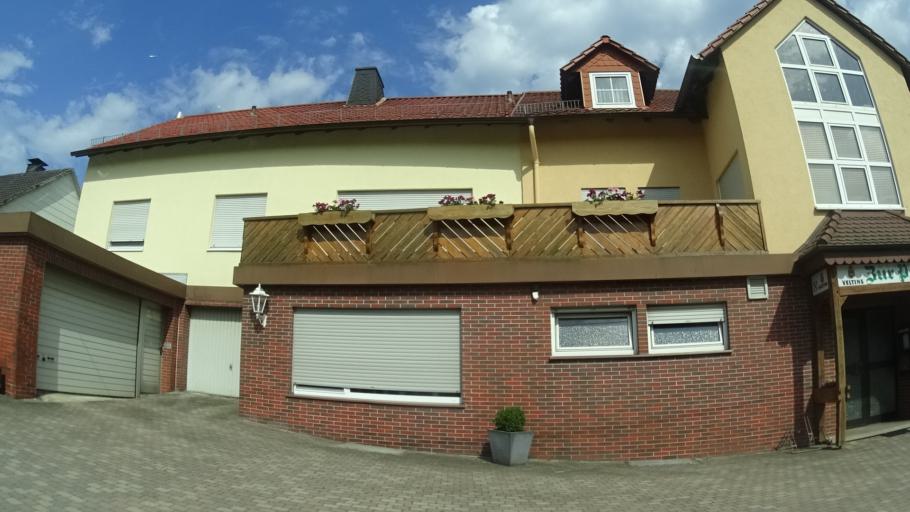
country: DE
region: Hesse
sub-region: Regierungsbezirk Kassel
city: Bad Wildungen
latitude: 51.1572
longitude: 9.1231
